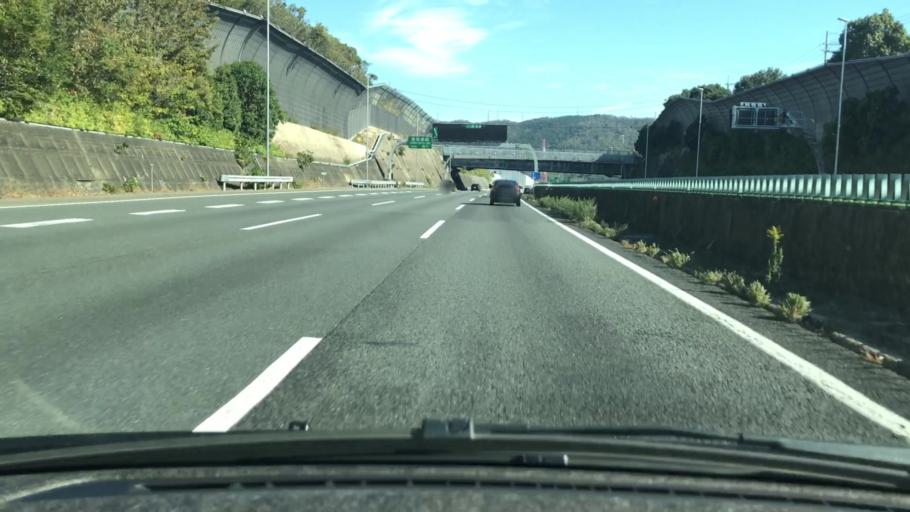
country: JP
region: Osaka
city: Takatsuki
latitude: 34.8661
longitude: 135.6136
